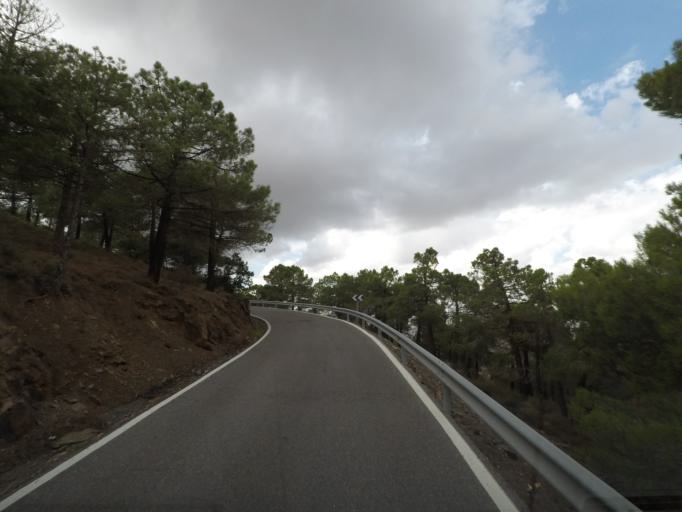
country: ES
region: Andalusia
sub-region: Provincia de Granada
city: Aldeire
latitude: 37.1624
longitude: -3.0536
